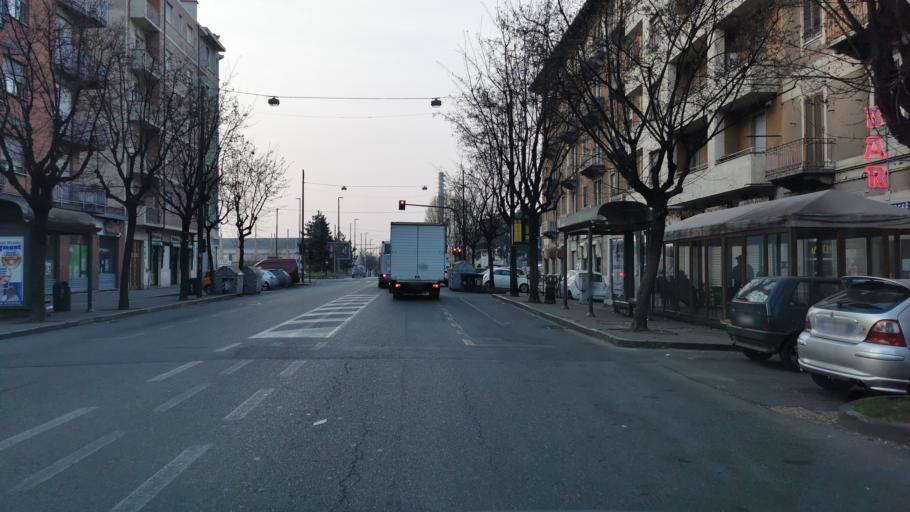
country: IT
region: Piedmont
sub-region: Provincia di Torino
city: Turin
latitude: 45.0963
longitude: 7.6630
